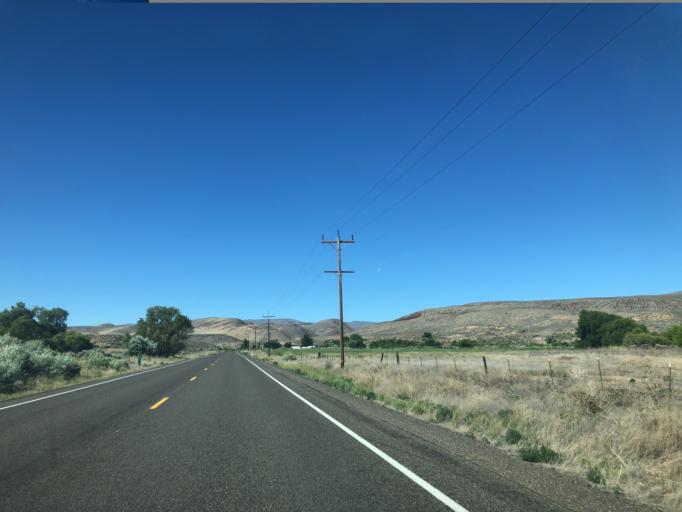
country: US
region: Oregon
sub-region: Malheur County
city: Vale
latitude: 43.8021
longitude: -117.6748
